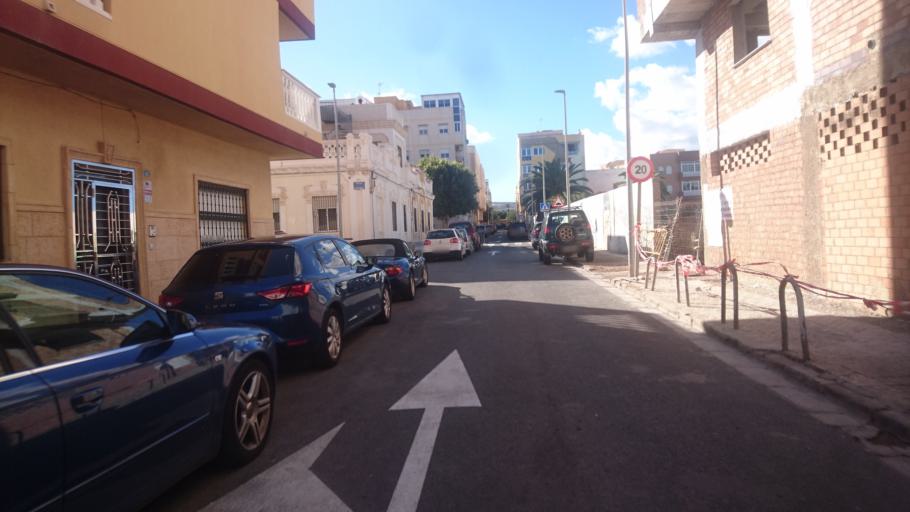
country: ES
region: Melilla
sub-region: Melilla
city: Melilla
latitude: 35.2765
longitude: -2.9447
